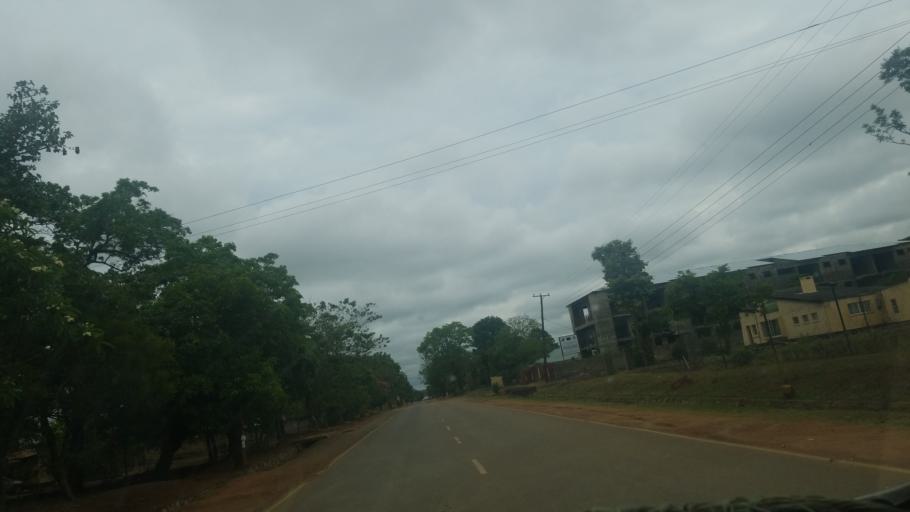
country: ZM
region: Luapula
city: Mansa
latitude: -11.1972
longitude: 28.8962
